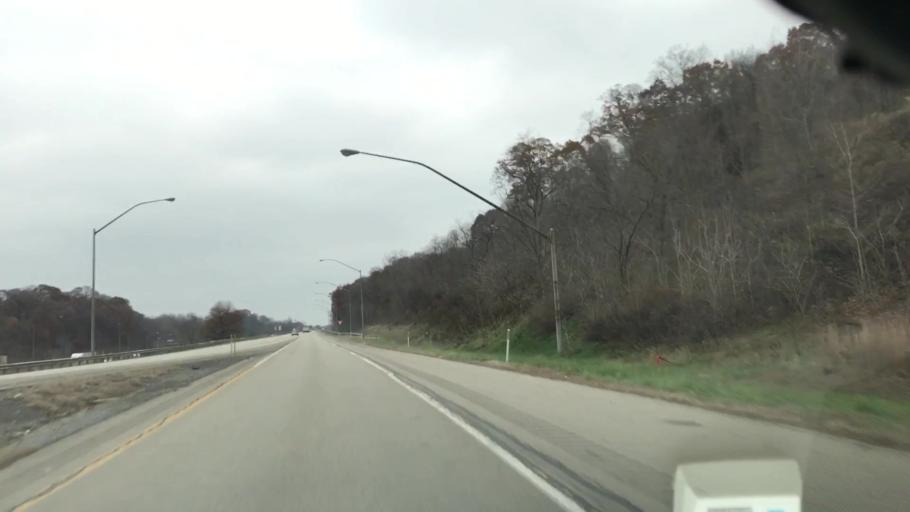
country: US
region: Pennsylvania
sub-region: Allegheny County
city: Coraopolis
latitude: 40.5015
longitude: -80.1349
